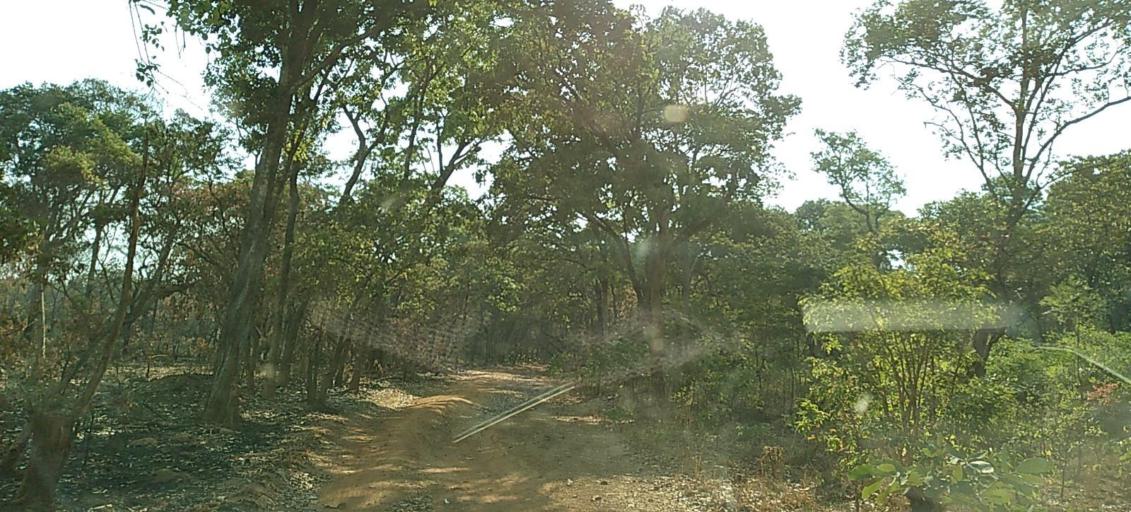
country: ZM
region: Copperbelt
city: Kalulushi
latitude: -13.0068
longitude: 27.7254
